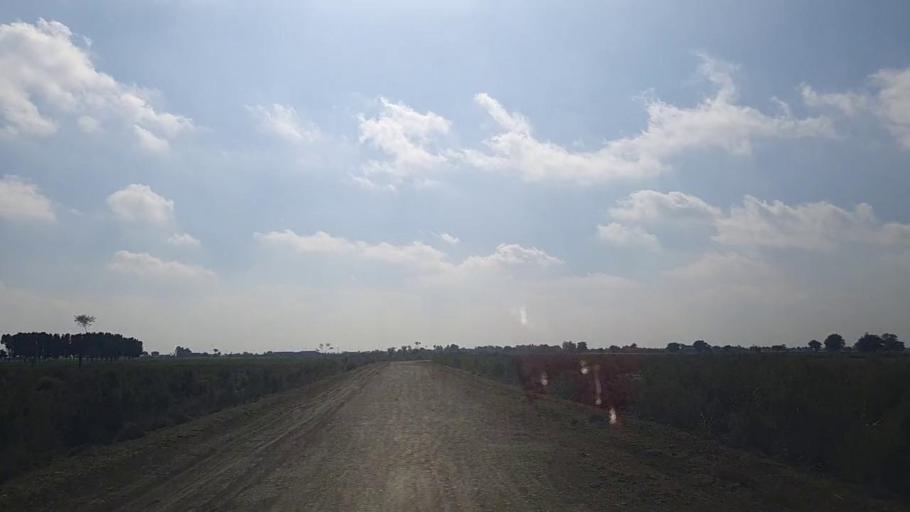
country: PK
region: Sindh
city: Sanghar
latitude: 26.0541
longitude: 69.0052
